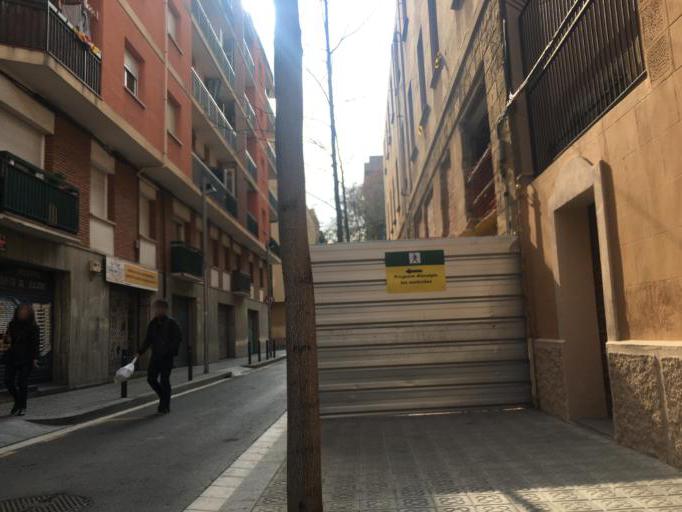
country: ES
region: Catalonia
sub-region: Provincia de Barcelona
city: les Corts
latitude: 41.3837
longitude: 2.1358
